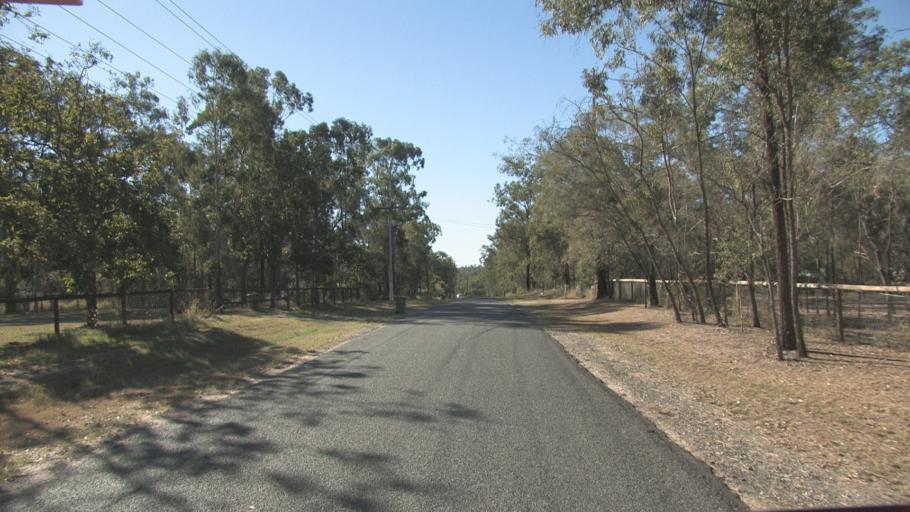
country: AU
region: Queensland
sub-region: Logan
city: Park Ridge South
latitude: -27.7272
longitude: 153.0121
